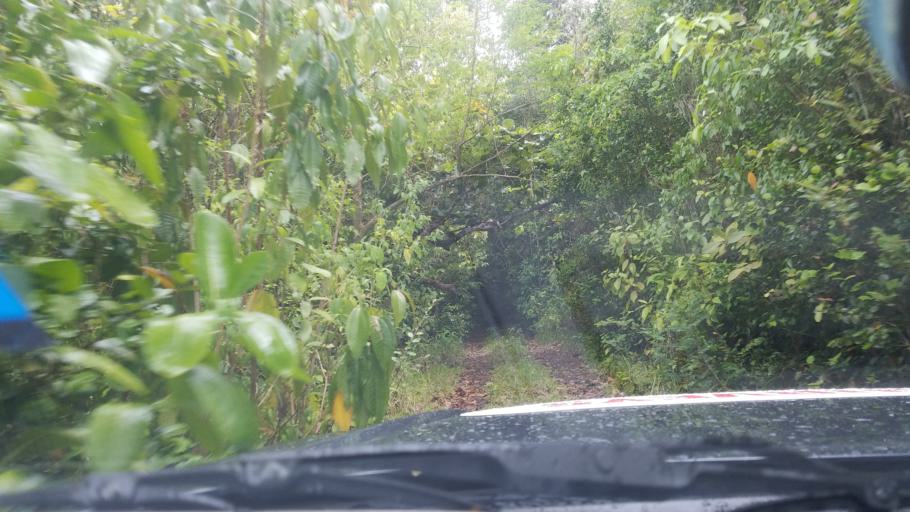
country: LC
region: Dennery Quarter
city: Dennery
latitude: 13.9746
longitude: -60.8943
